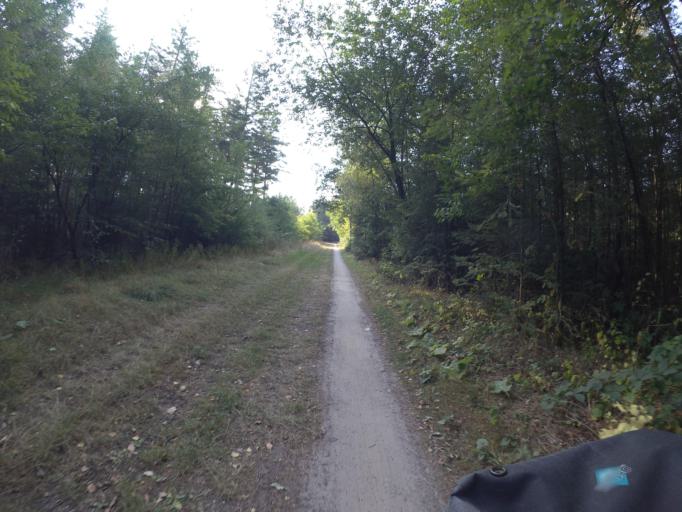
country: NL
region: Drenthe
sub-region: Gemeente Westerveld
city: Dwingeloo
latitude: 52.9184
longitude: 6.3338
